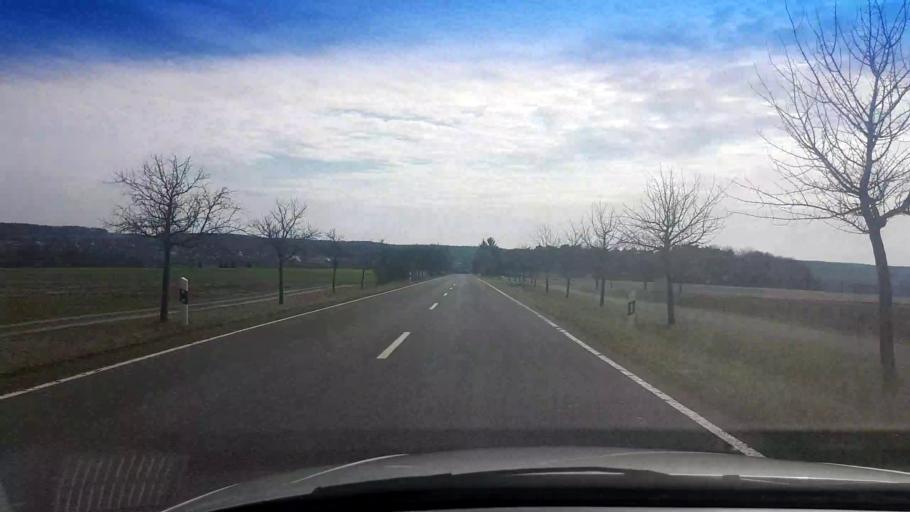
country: DE
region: Bavaria
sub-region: Upper Franconia
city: Frensdorf
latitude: 49.8309
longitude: 10.8689
